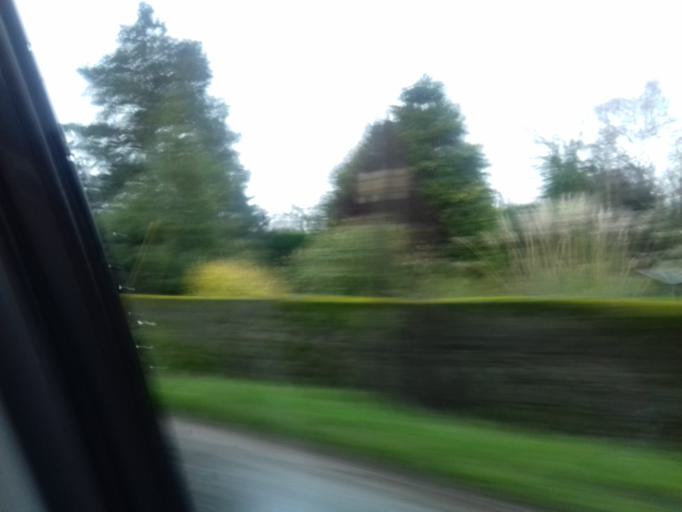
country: IE
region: Leinster
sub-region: County Carlow
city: Bagenalstown
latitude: 52.6524
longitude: -6.9894
